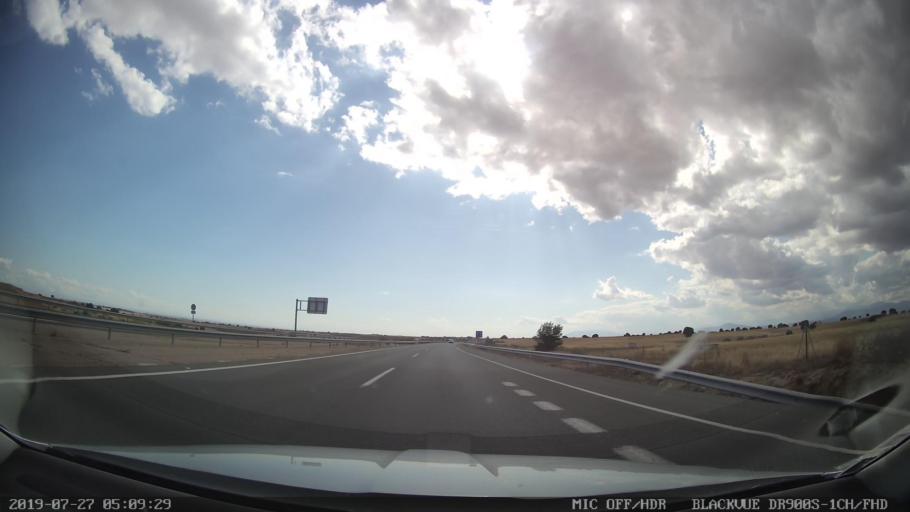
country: ES
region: Castille-La Mancha
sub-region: Province of Toledo
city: Santa Cruz del Retamar
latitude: 40.1183
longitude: -4.2662
